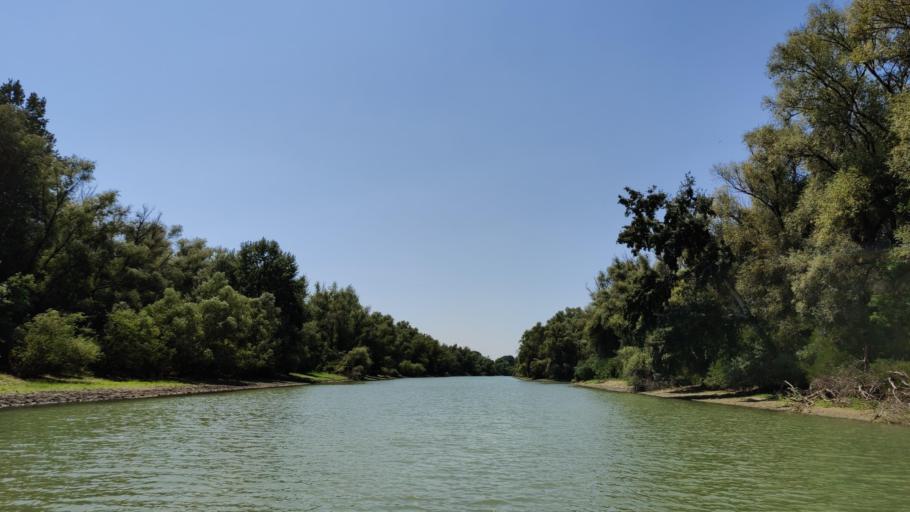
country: RO
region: Tulcea
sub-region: Comuna Nufaru
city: Nufaru
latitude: 45.2242
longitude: 28.8850
